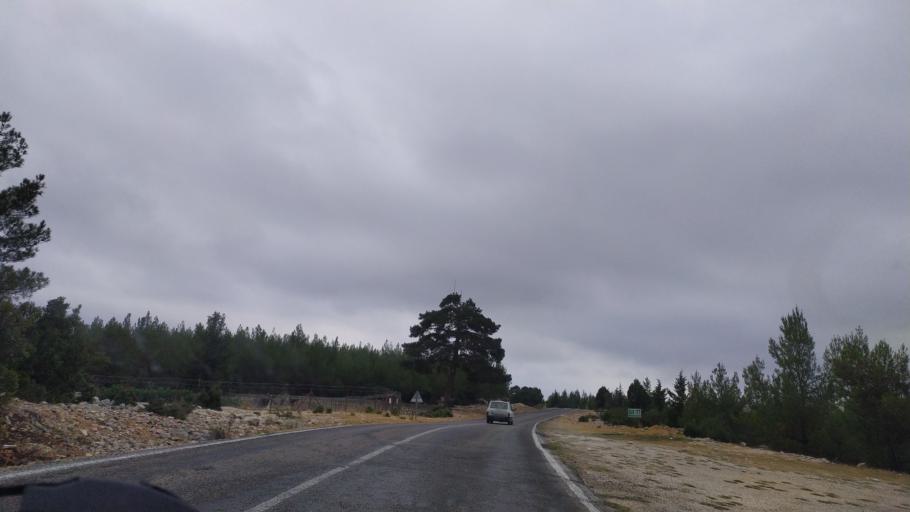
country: TR
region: Mersin
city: Silifke
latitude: 36.5420
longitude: 33.9279
